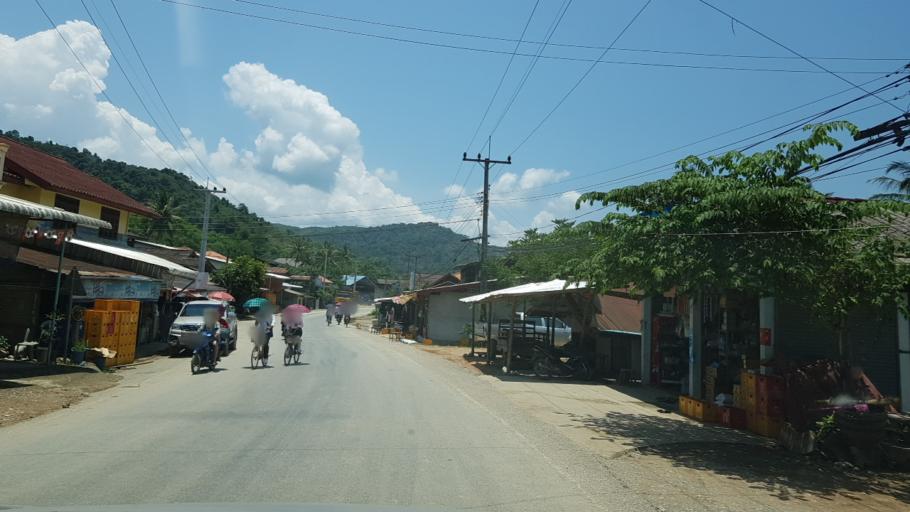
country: LA
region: Vientiane
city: Muang Kasi
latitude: 19.2334
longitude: 102.2525
